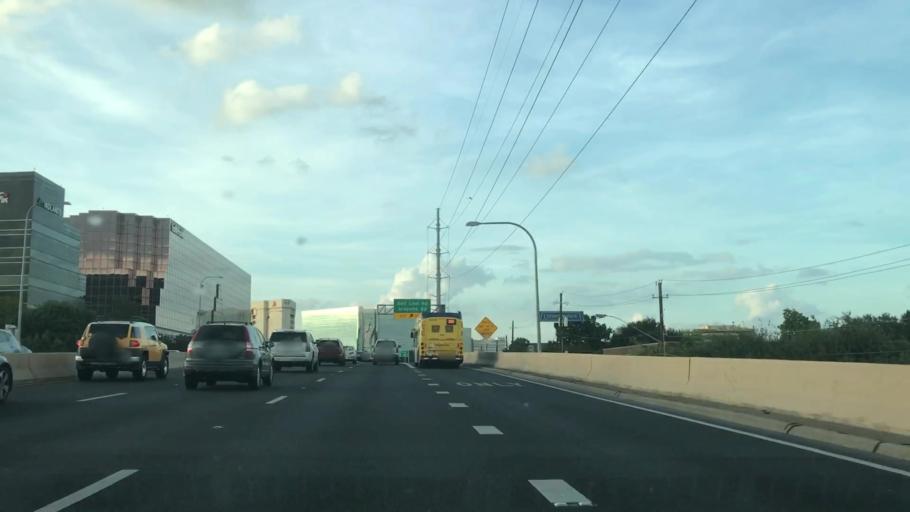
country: US
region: Texas
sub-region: Dallas County
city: Addison
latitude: 32.9472
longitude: -96.8232
